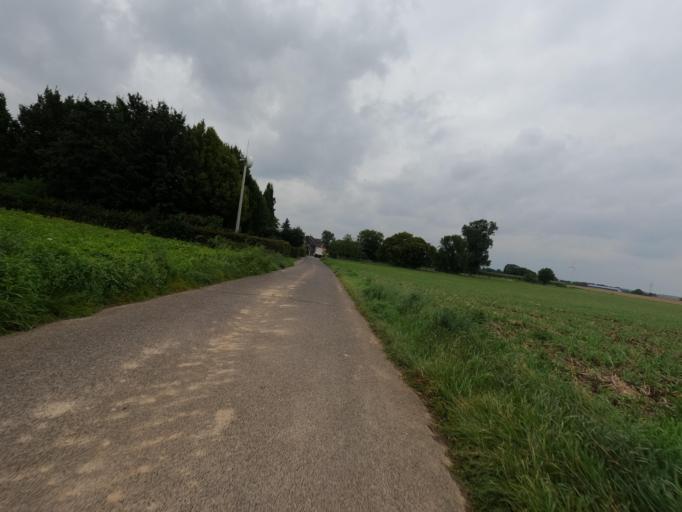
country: DE
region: North Rhine-Westphalia
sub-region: Regierungsbezirk Koln
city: Linnich
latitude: 50.9942
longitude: 6.2181
